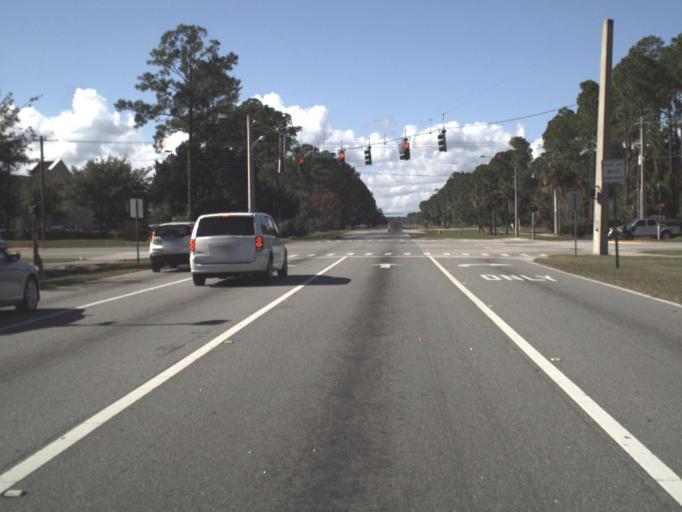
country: US
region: Florida
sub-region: Flagler County
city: Palm Coast
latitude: 29.5534
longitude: -81.2364
